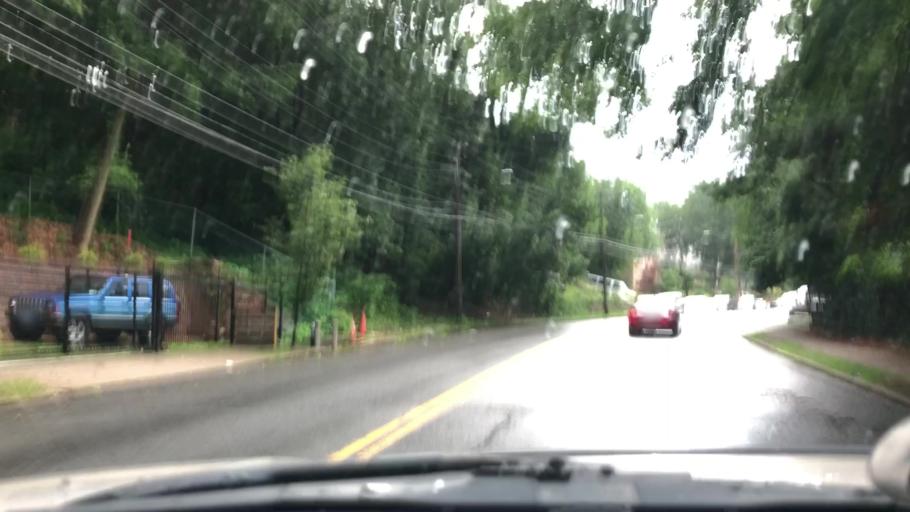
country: US
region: New Jersey
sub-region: Hudson County
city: Bayonne
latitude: 40.6350
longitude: -74.0936
